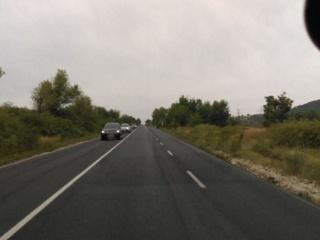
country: BG
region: Plovdiv
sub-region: Obshtina Karlovo
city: Karlovo
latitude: 42.5210
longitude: 24.8127
